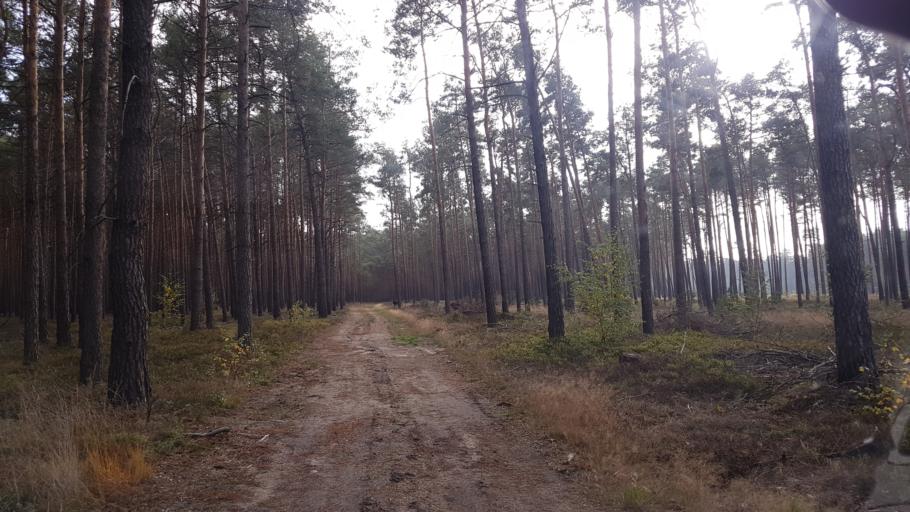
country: DE
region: Brandenburg
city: Schonborn
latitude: 51.6603
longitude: 13.4793
